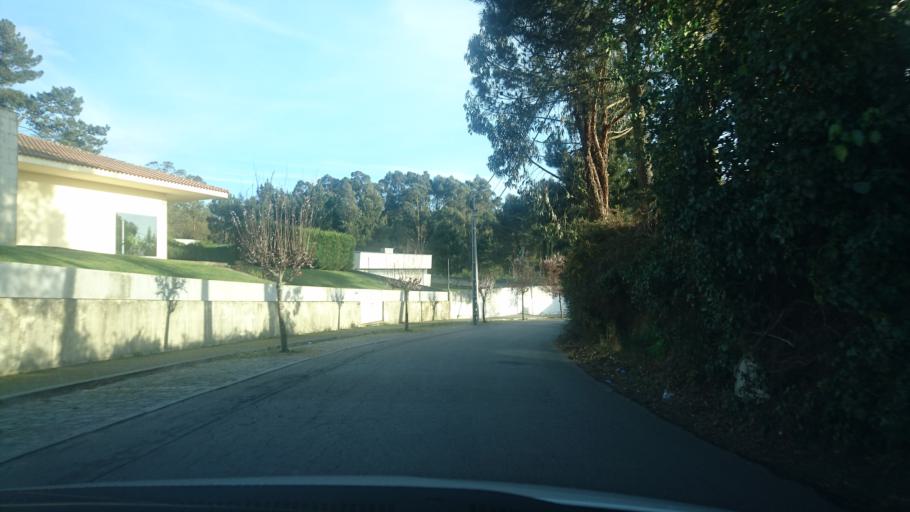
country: PT
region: Aveiro
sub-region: Santa Maria da Feira
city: Nogueira da Regedoura
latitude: 41.0032
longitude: -8.6058
